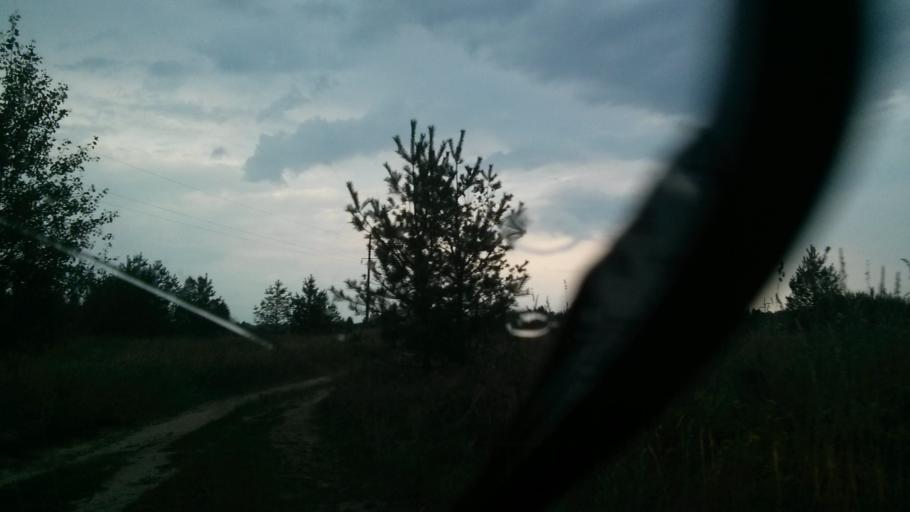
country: RU
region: Nizjnij Novgorod
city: Shimorskoye
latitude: 55.3171
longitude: 41.8625
